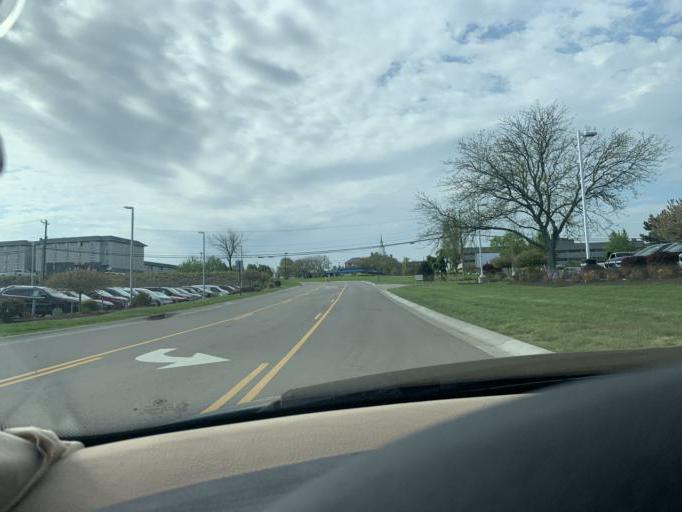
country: US
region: Ohio
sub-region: Hamilton County
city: Springdale
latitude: 39.2863
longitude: -84.4706
